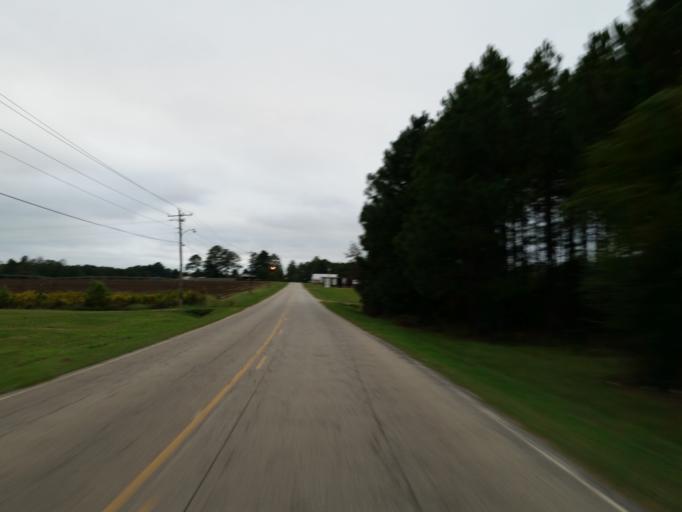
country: US
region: Georgia
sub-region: Crisp County
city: Cordele
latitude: 31.8356
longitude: -83.7242
